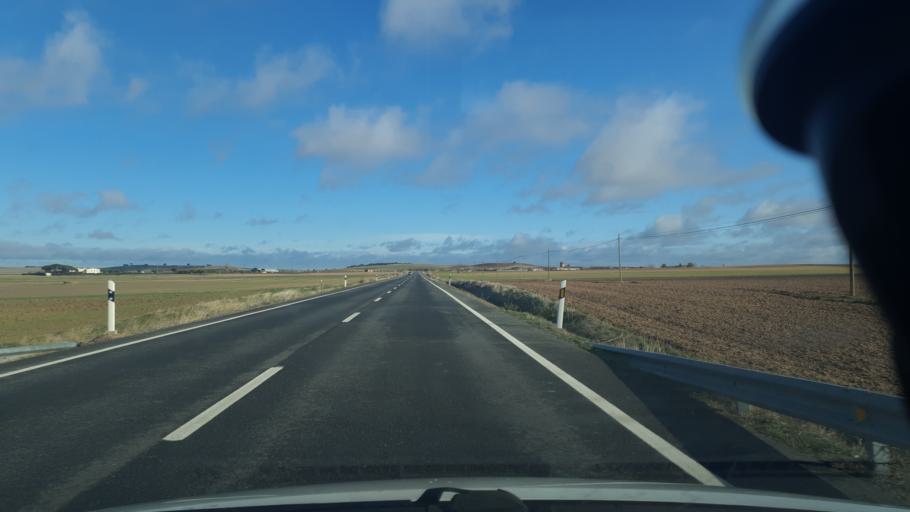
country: ES
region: Castille and Leon
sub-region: Provincia de Segovia
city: Codorniz
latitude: 41.0581
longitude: -4.6159
